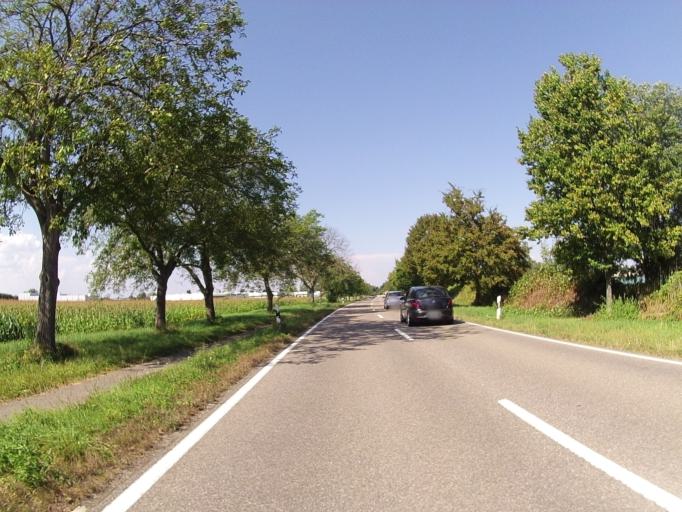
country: DE
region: Rheinland-Pfalz
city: Neuburg
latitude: 49.0040
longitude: 8.2595
